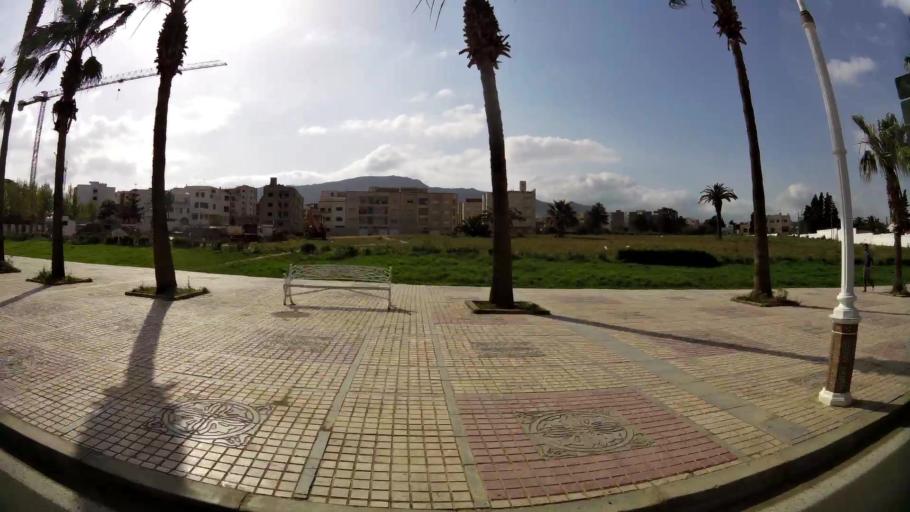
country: MA
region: Tanger-Tetouan
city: Tetouan
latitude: 35.5897
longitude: -5.3454
